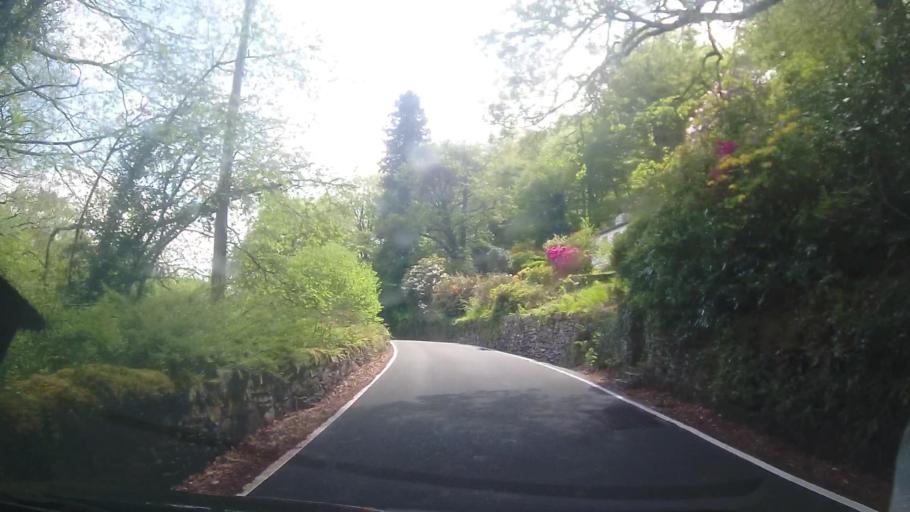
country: GB
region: Wales
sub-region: Gwynedd
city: Penrhyndeudraeth
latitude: 52.9916
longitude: -4.0965
